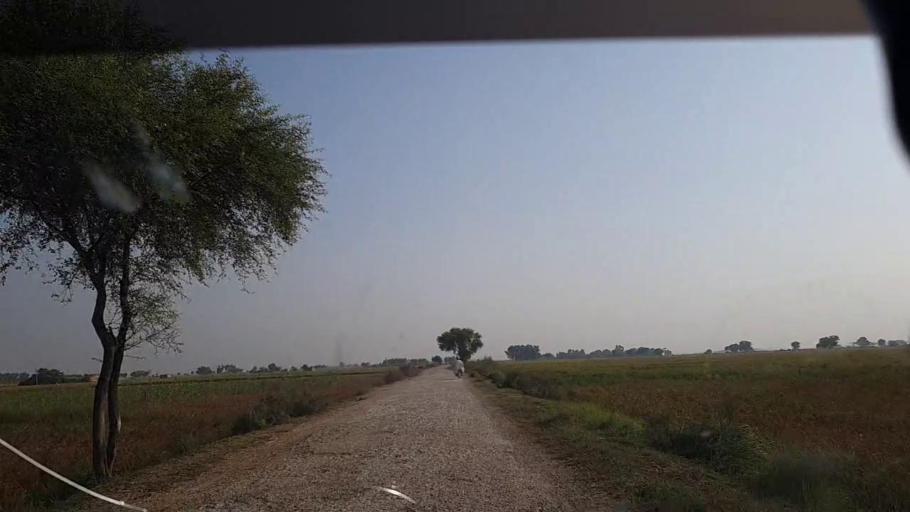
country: PK
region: Sindh
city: Shikarpur
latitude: 28.0696
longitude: 68.5459
